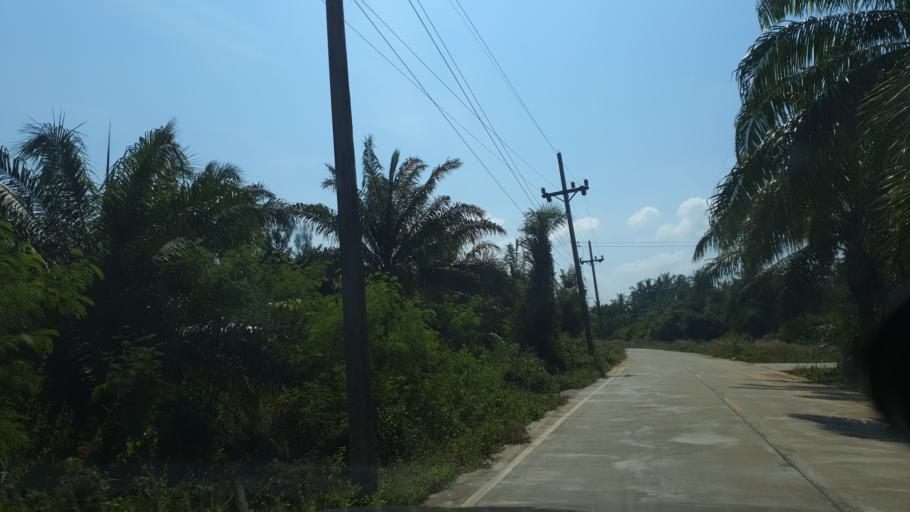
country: TH
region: Surat Thani
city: Tha Chana
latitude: 9.5935
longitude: 99.2037
